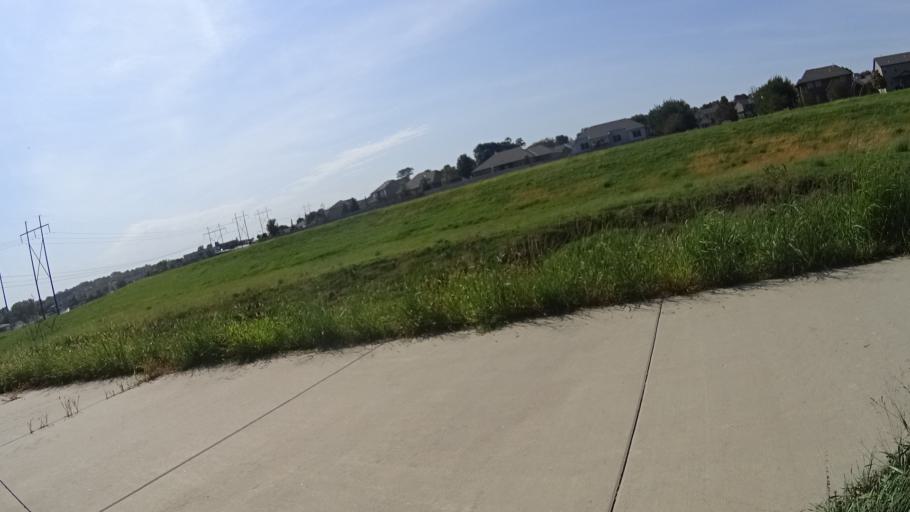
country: US
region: Nebraska
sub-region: Sarpy County
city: Offutt Air Force Base
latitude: 41.1457
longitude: -95.9773
